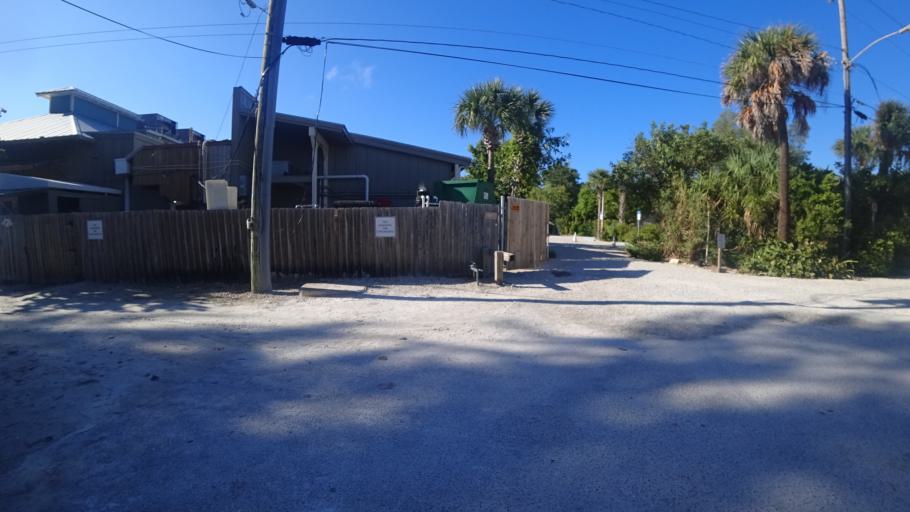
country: US
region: Florida
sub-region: Manatee County
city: Anna Maria
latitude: 27.5255
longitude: -82.7366
